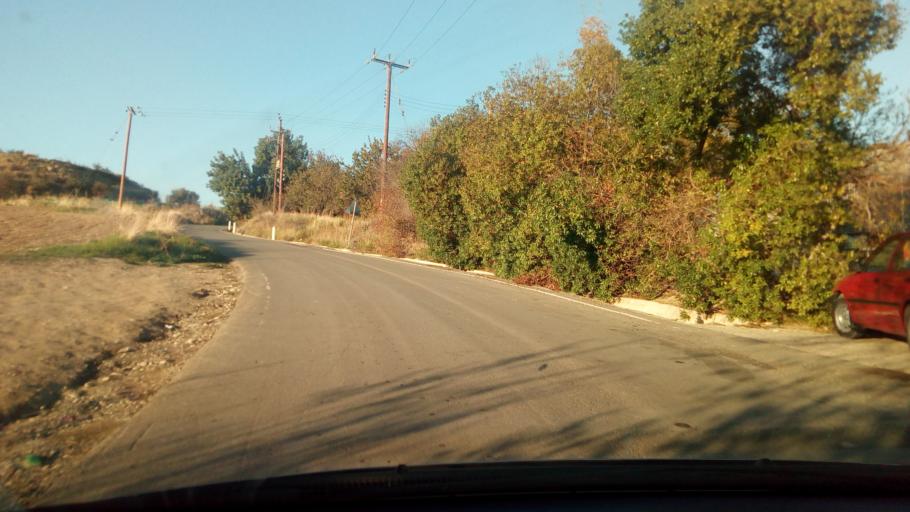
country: CY
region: Pafos
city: Polis
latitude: 34.9795
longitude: 32.4640
